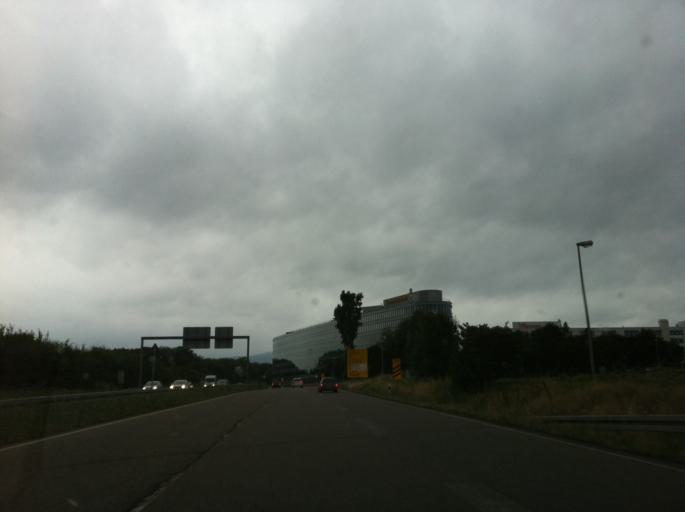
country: DE
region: Hesse
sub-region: Regierungsbezirk Darmstadt
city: Eschborn
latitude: 50.1360
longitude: 8.5834
